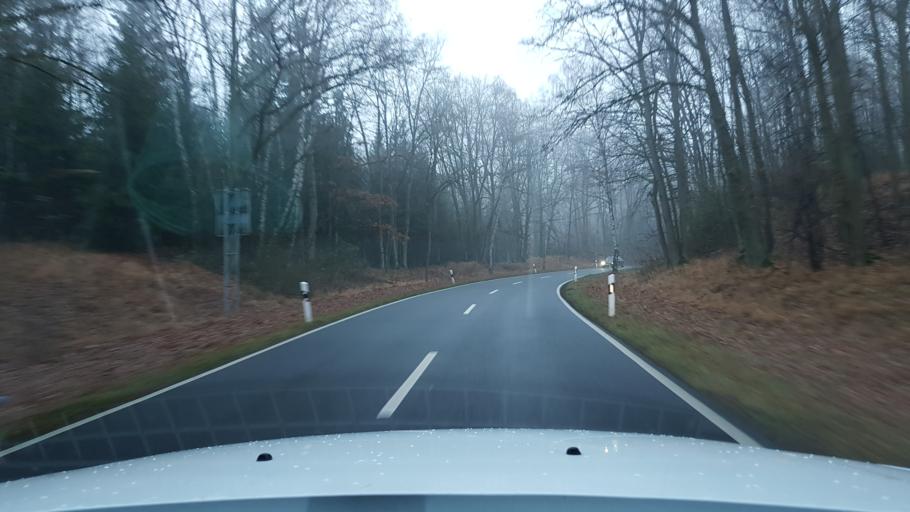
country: DE
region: Brandenburg
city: Mescherin
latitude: 53.2610
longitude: 14.4329
